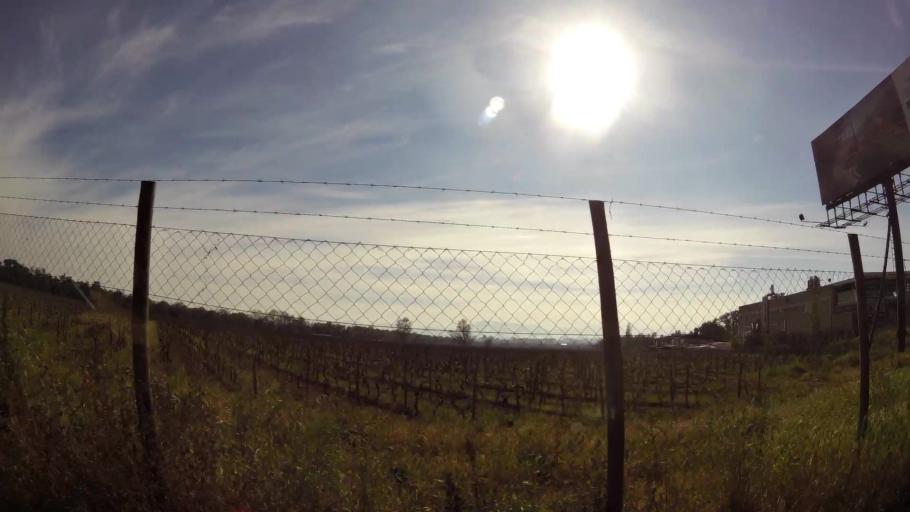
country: CL
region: Santiago Metropolitan
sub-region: Provincia de Santiago
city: Villa Presidente Frei, Nunoa, Santiago, Chile
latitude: -33.4880
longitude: -70.5587
